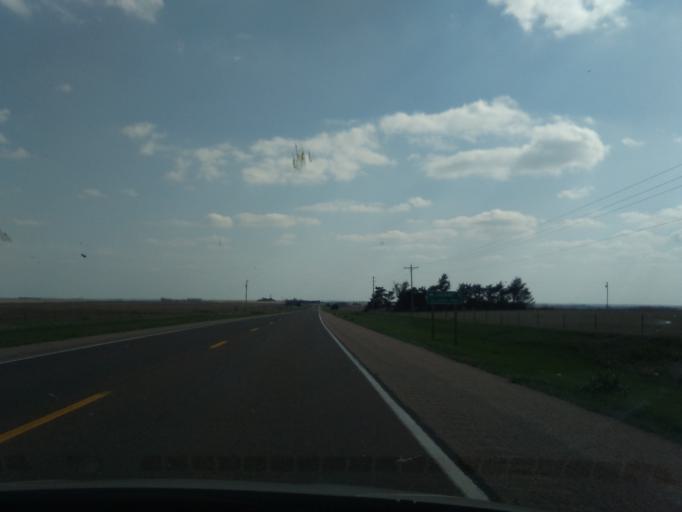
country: US
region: Nebraska
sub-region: Nuckolls County
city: Superior
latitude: 40.1059
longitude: -98.0670
